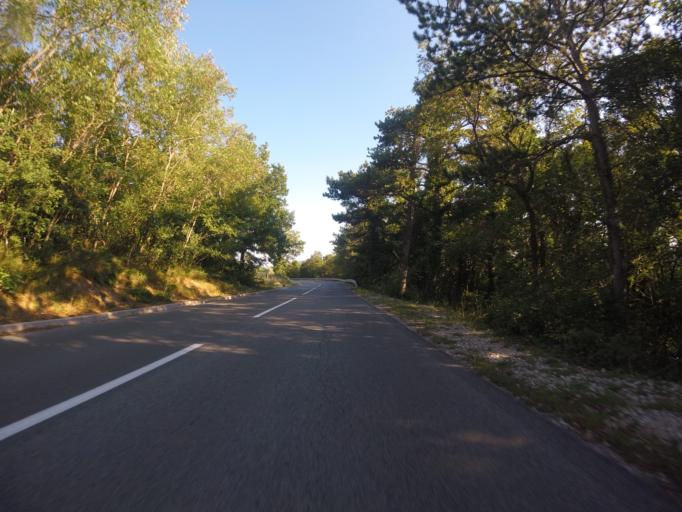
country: HR
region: Primorsko-Goranska
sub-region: Grad Crikvenica
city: Crikvenica
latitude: 45.2066
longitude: 14.7134
